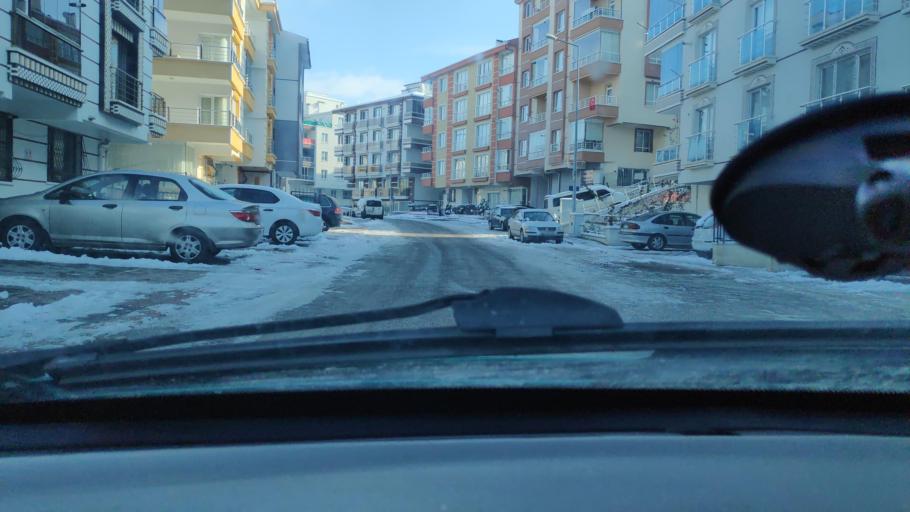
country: TR
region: Ankara
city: Ankara
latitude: 40.0115
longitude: 32.8442
